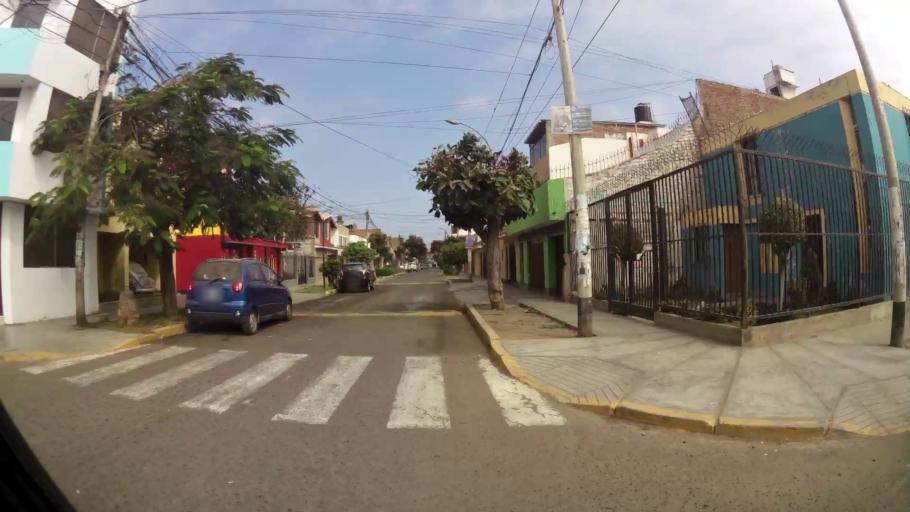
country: PE
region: La Libertad
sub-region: Provincia de Trujillo
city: Trujillo
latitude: -8.1199
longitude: -79.0227
